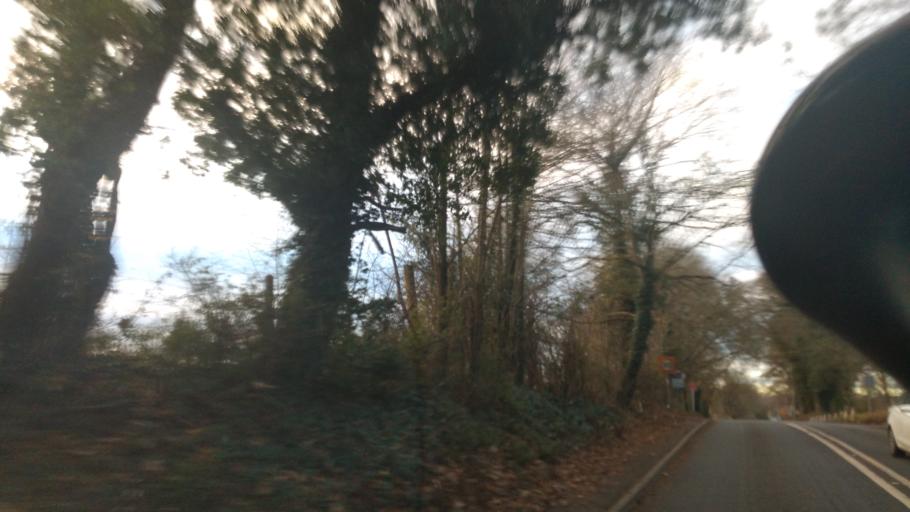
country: GB
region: England
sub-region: Somerset
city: Frome
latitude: 51.2453
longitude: -2.3107
